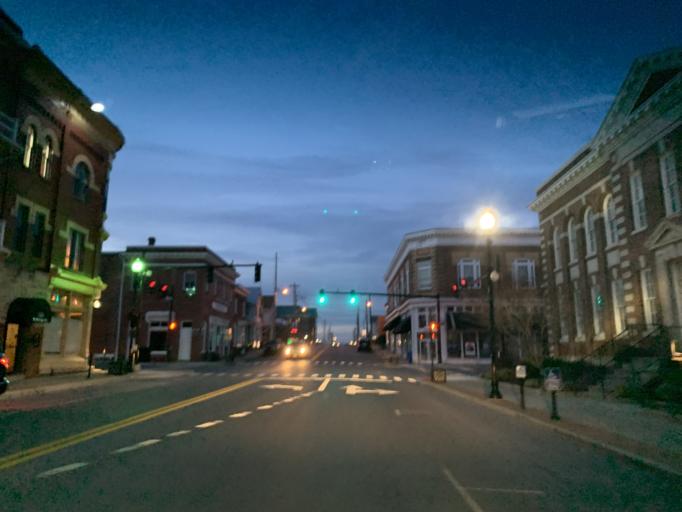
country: US
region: West Virginia
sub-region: Jefferson County
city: Charles Town
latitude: 39.2895
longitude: -77.8602
